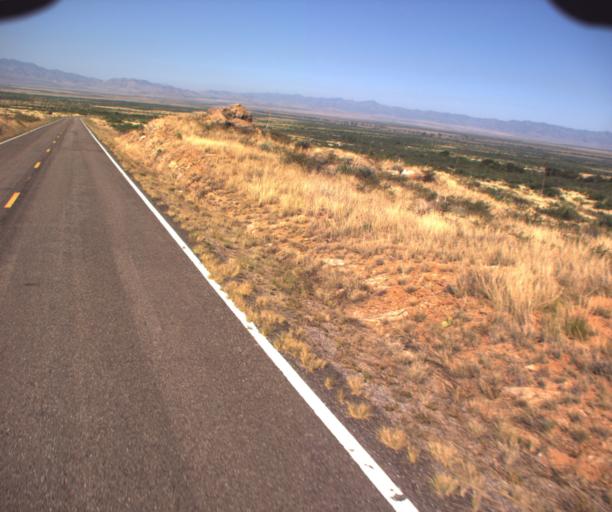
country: US
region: Arizona
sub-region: Graham County
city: Swift Trail Junction
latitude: 32.5970
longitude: -109.8956
